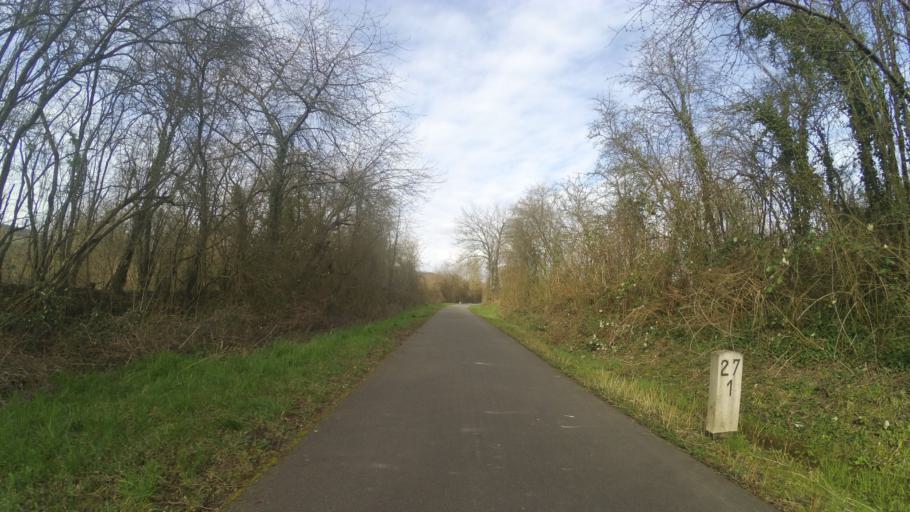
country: FR
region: Lorraine
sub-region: Departement de la Moselle
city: Bliesbruck
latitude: 49.1322
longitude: 7.1866
